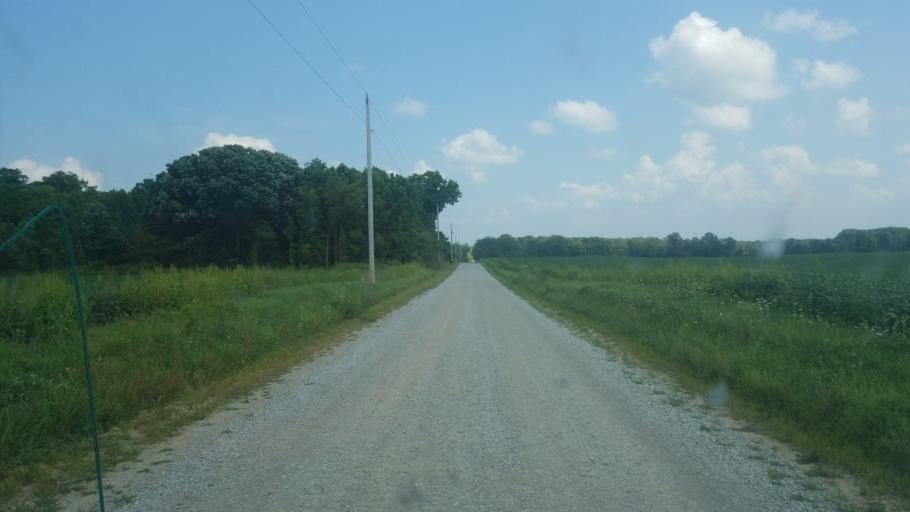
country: US
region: Ohio
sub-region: Huron County
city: New London
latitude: 41.0495
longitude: -82.3747
